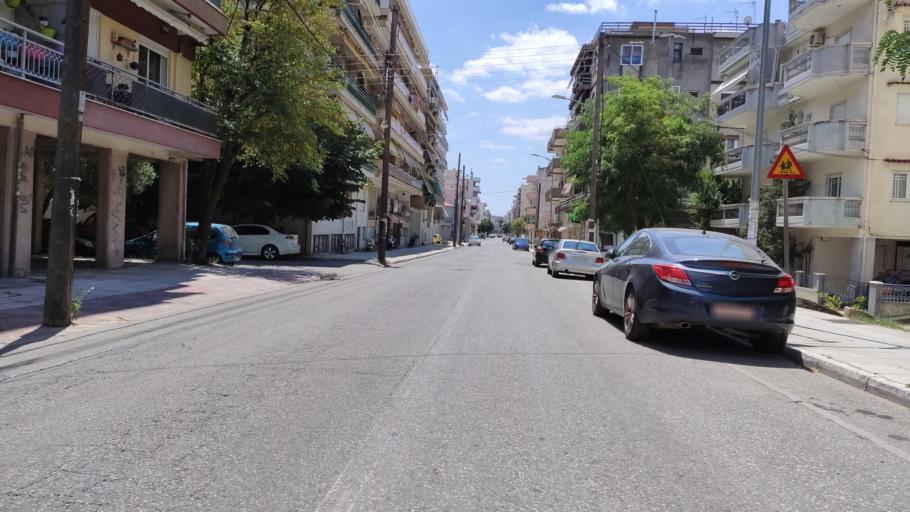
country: GR
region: East Macedonia and Thrace
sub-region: Nomos Rodopis
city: Komotini
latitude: 41.1262
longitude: 25.4112
